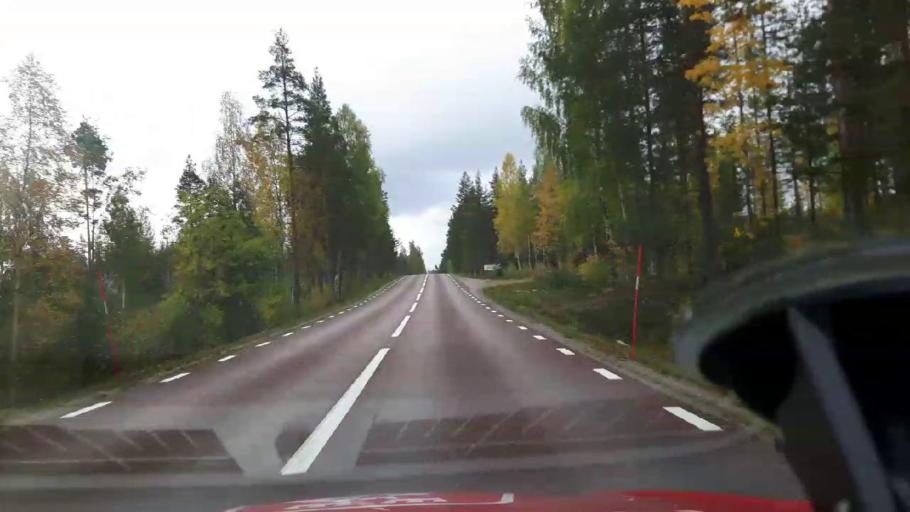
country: SE
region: Jaemtland
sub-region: Harjedalens Kommun
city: Sveg
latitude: 62.2060
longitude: 14.8479
